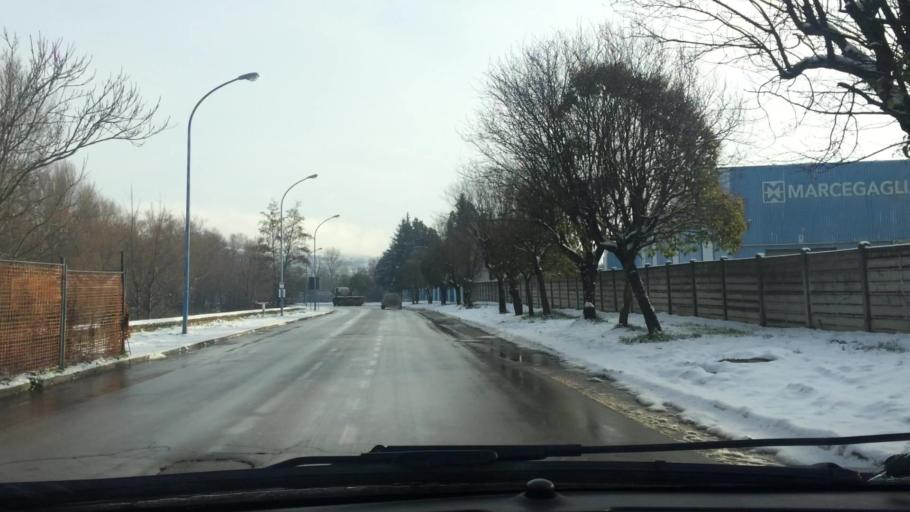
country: IT
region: Basilicate
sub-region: Provincia di Potenza
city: Potenza
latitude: 40.6315
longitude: 15.8147
